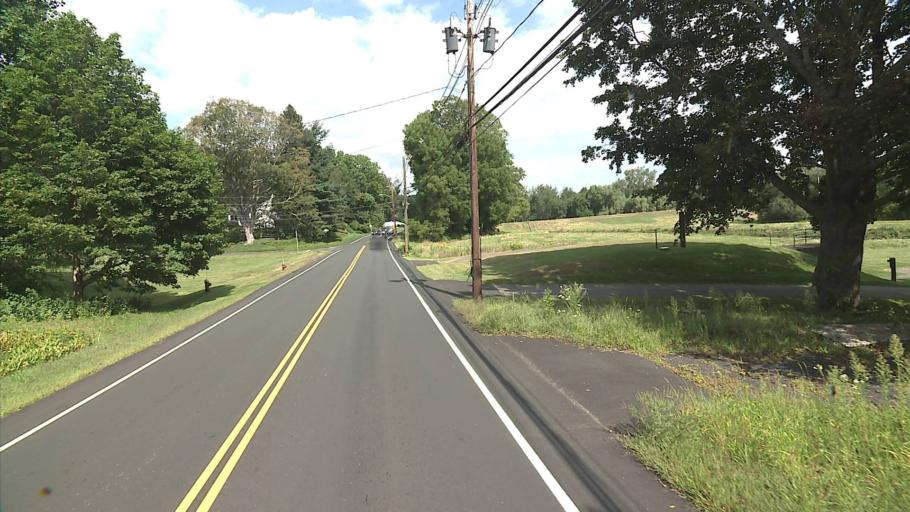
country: US
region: Connecticut
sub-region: Hartford County
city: West Hartford
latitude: 41.8180
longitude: -72.7670
